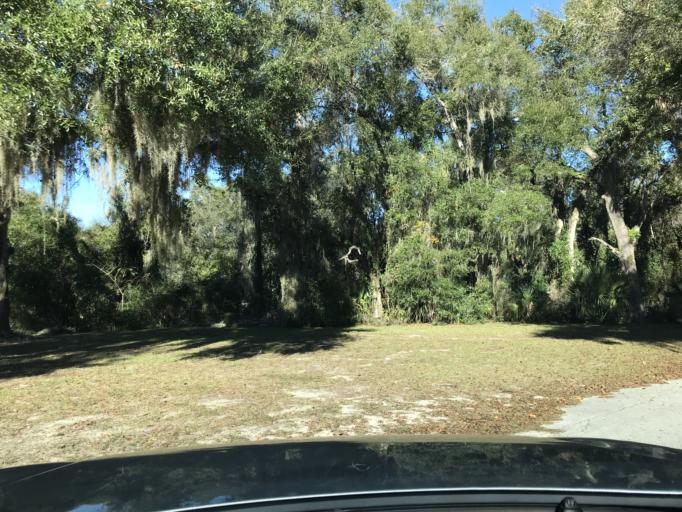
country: US
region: Florida
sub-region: Sumter County
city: Lake Panasoffkee
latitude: 28.7564
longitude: -82.0975
